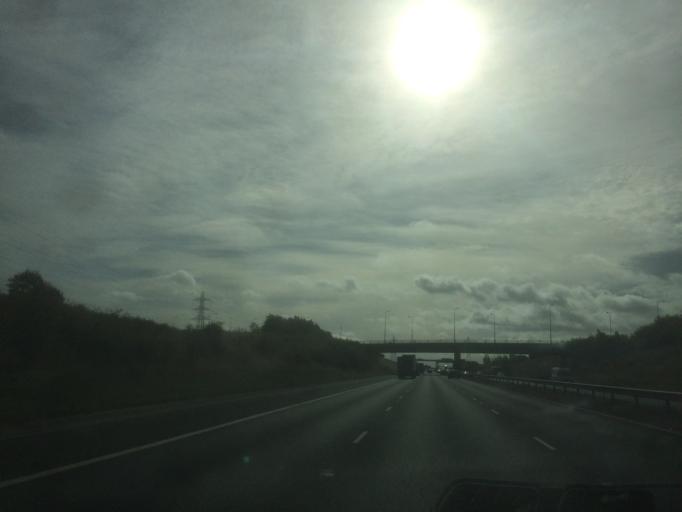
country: GB
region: England
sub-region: City and Borough of Leeds
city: Ledsham
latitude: 53.7651
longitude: -1.2837
